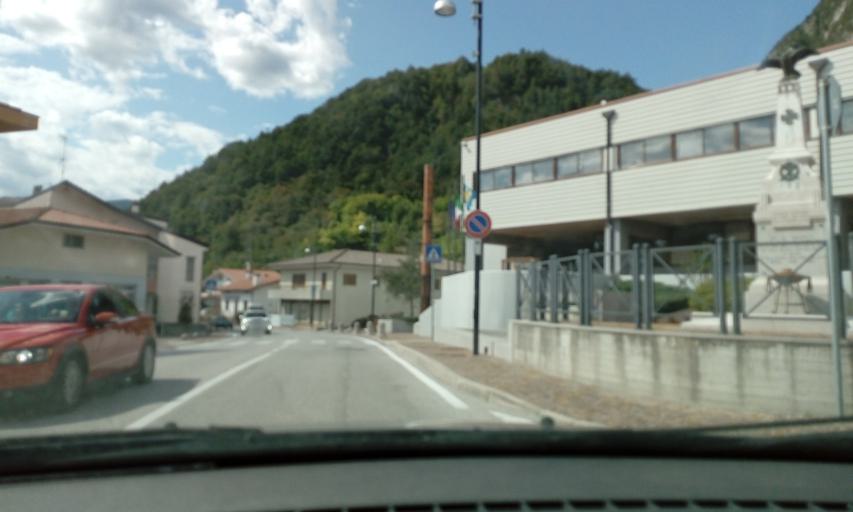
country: IT
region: Friuli Venezia Giulia
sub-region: Provincia di Udine
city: Trasaghis
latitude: 46.2822
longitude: 13.0756
